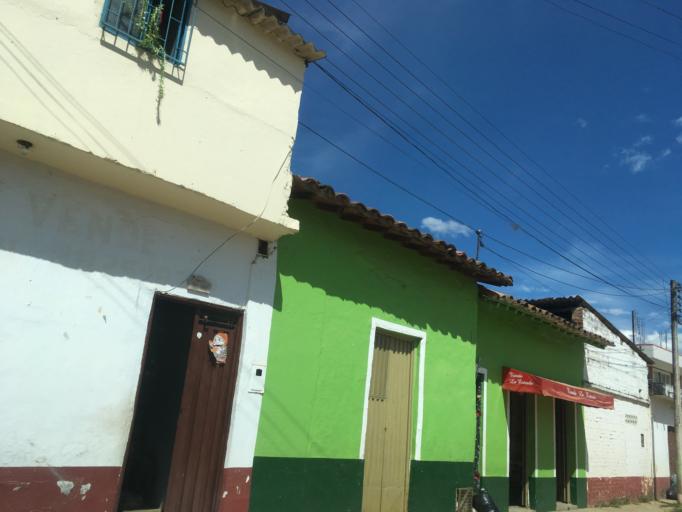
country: CO
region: Santander
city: Coromoro
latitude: 6.2869
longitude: -73.1505
